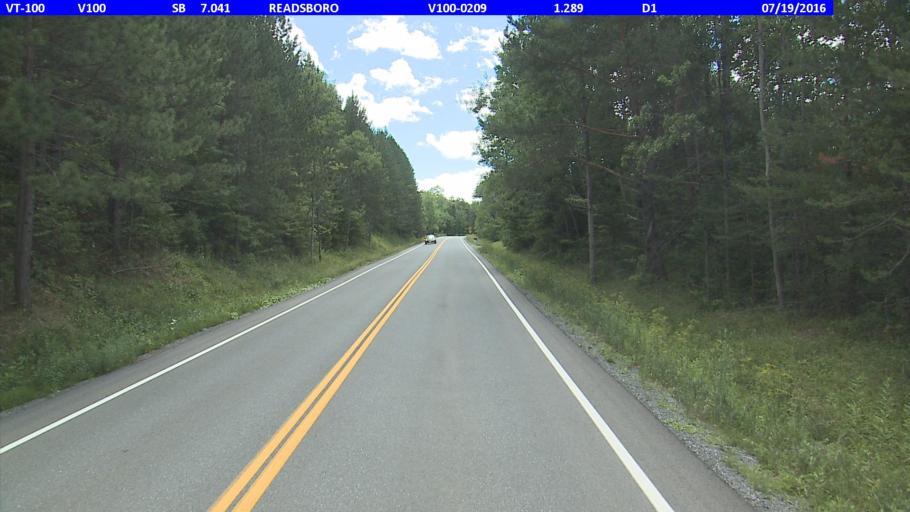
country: US
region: Massachusetts
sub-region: Berkshire County
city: North Adams
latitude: 42.8242
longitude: -73.0029
